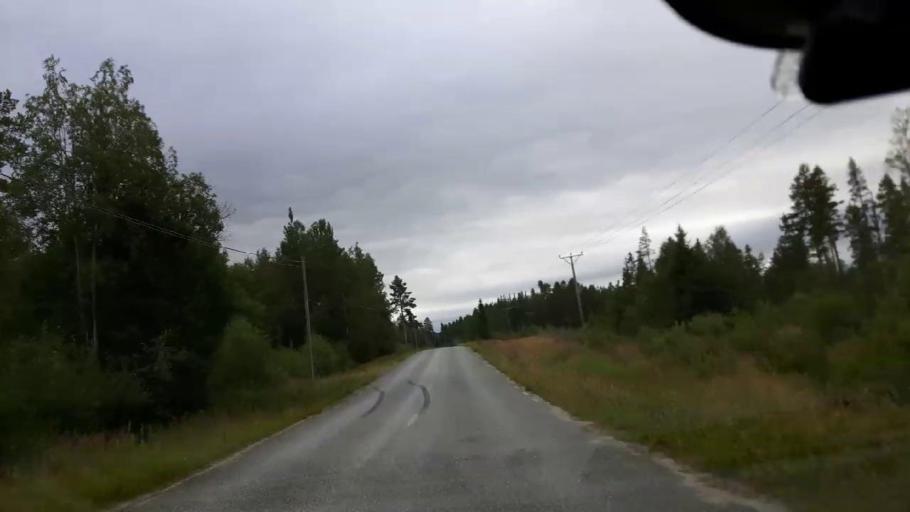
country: SE
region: Jaemtland
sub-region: Braecke Kommun
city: Braecke
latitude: 62.8832
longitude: 15.6187
